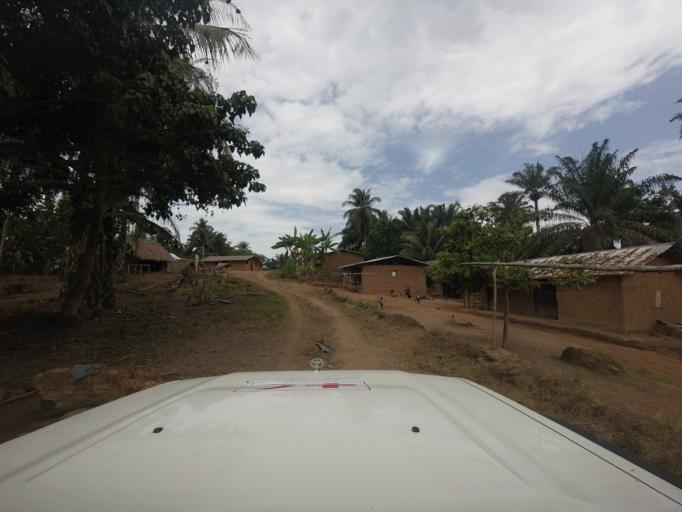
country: SL
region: Eastern Province
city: Buedu
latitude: 8.2476
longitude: -10.2522
